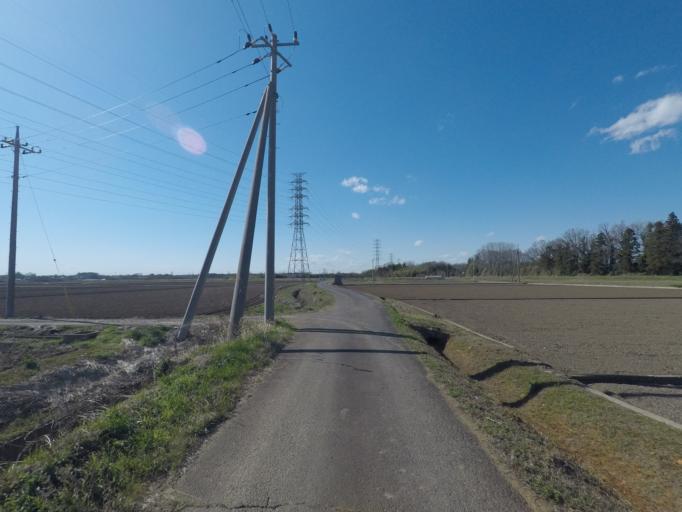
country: JP
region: Ibaraki
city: Tsukuba
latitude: 36.1417
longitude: 140.1135
